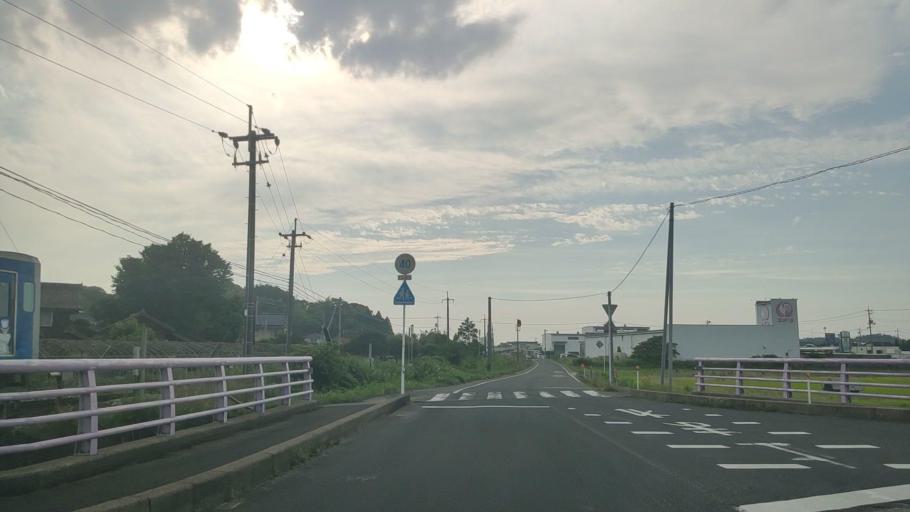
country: JP
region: Tottori
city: Kurayoshi
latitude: 35.4801
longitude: 133.8145
